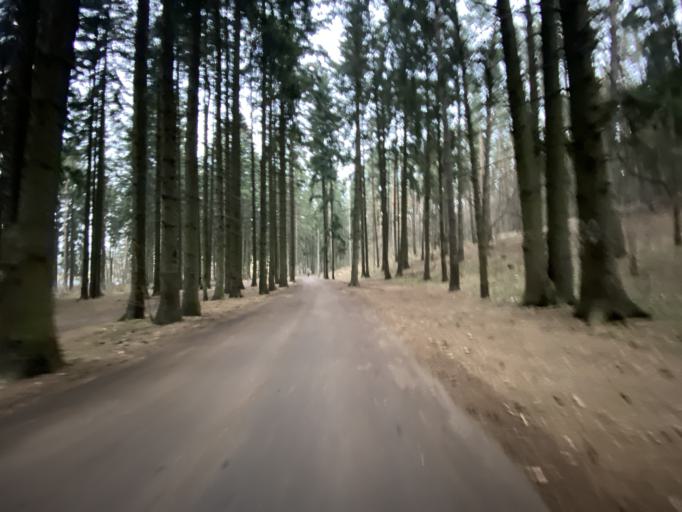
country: BY
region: Minsk
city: Borovlyany
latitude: 53.9462
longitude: 27.6519
